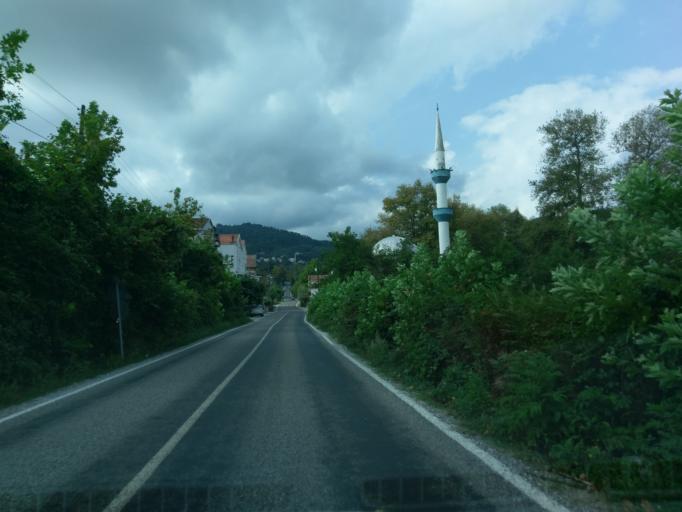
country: TR
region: Sinop
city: Helaldi
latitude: 41.9257
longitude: 34.4155
